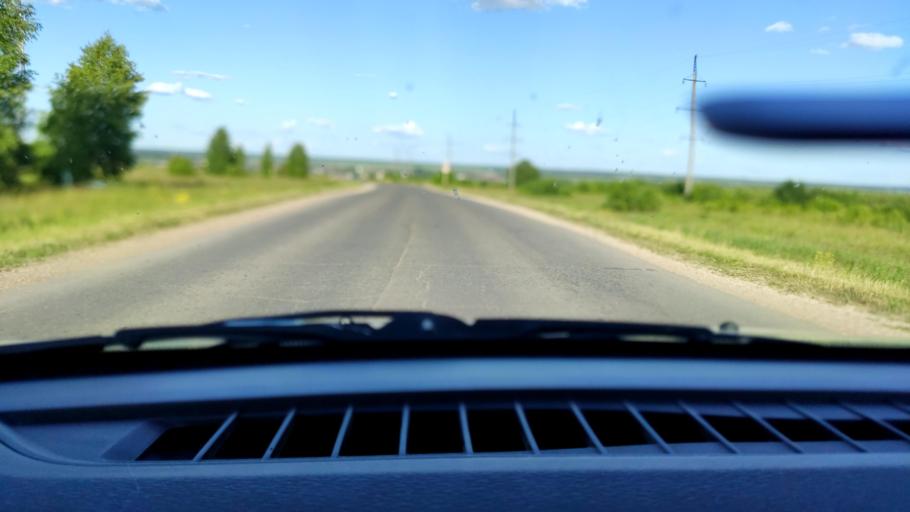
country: RU
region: Perm
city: Orda
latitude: 57.1884
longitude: 56.8769
